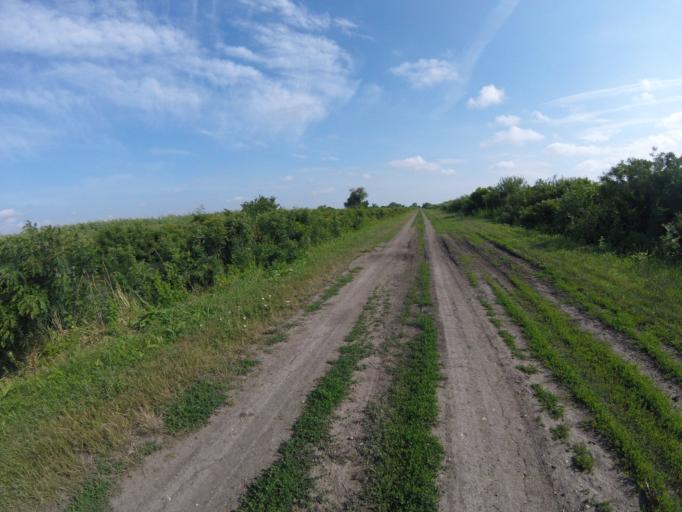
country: HU
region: Hajdu-Bihar
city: Hortobagy
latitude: 47.6231
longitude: 21.0777
